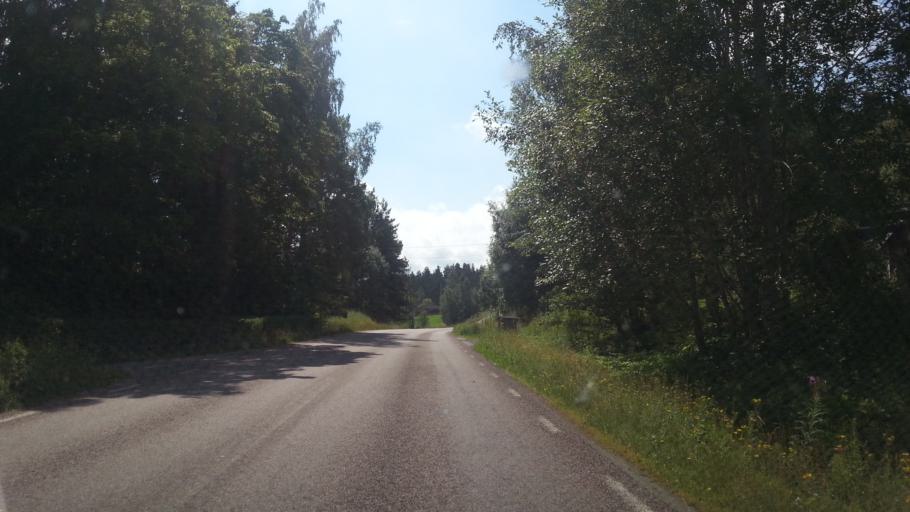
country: SE
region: Dalarna
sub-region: Faluns Kommun
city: Falun
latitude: 60.6217
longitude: 15.7670
